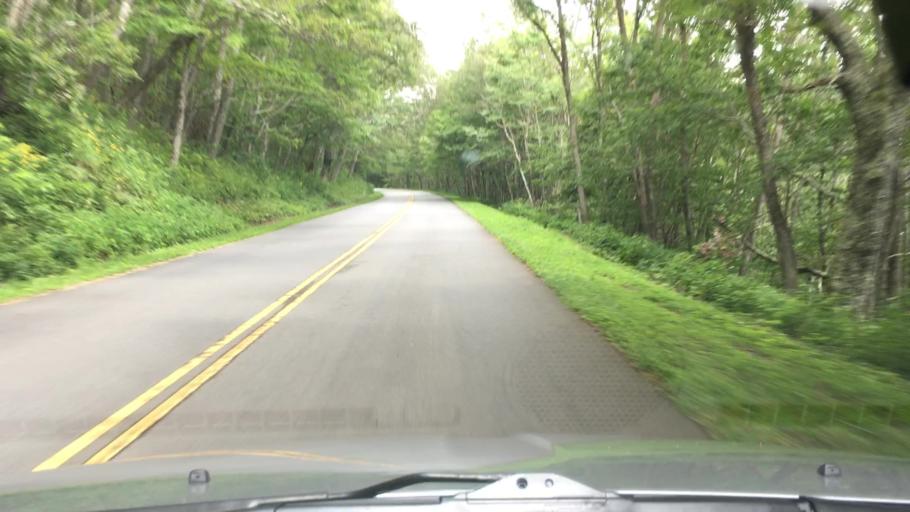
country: US
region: North Carolina
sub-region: Buncombe County
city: Swannanoa
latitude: 35.6958
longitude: -82.4071
